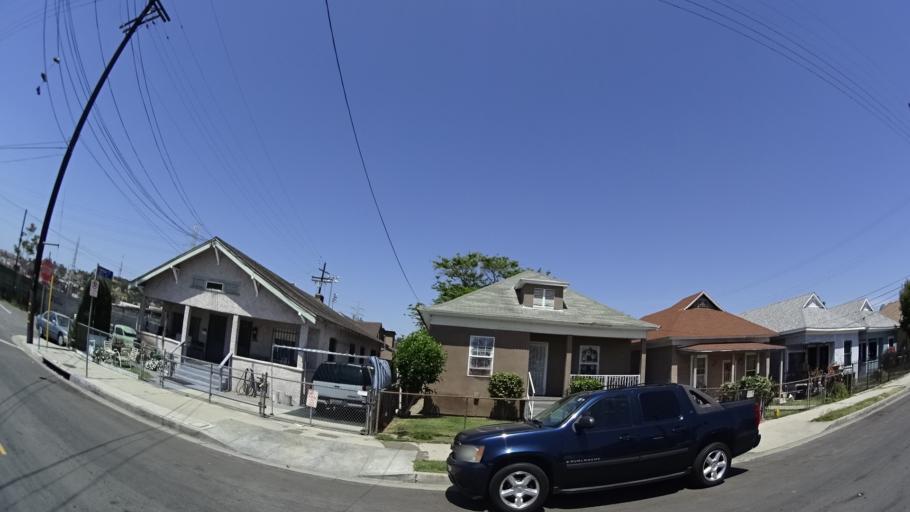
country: US
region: California
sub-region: Los Angeles County
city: Los Angeles
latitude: 34.0692
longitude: -118.2222
